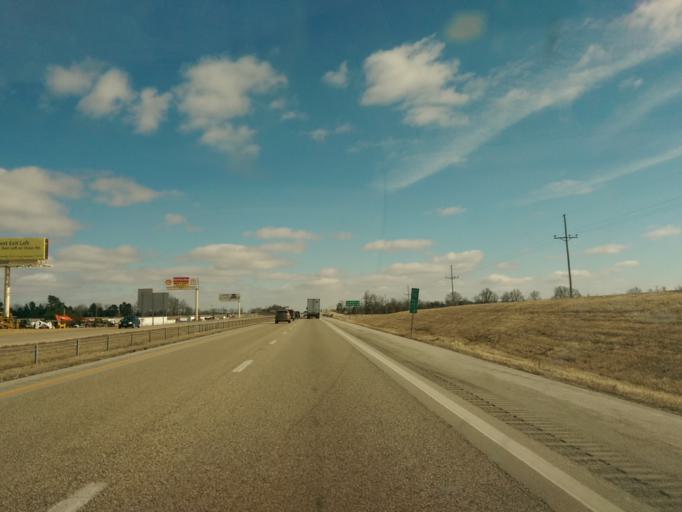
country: US
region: Missouri
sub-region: Montgomery County
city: Montgomery City
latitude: 38.9073
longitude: -91.5251
